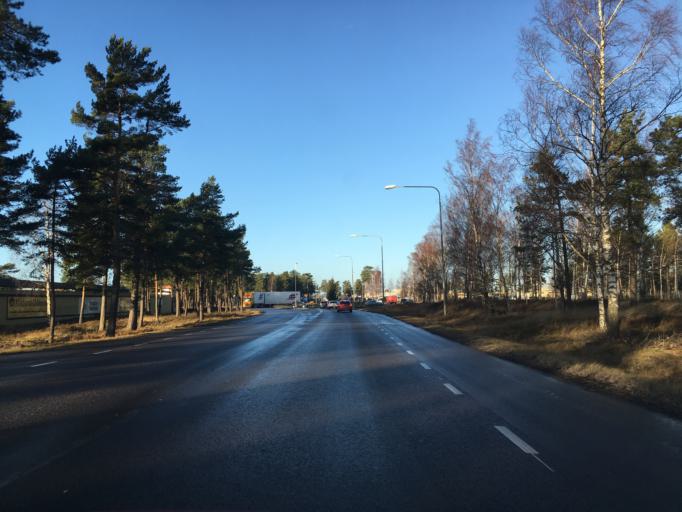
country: SE
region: Kalmar
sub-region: Vasterviks Kommun
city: Vaestervik
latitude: 57.7642
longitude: 16.6023
